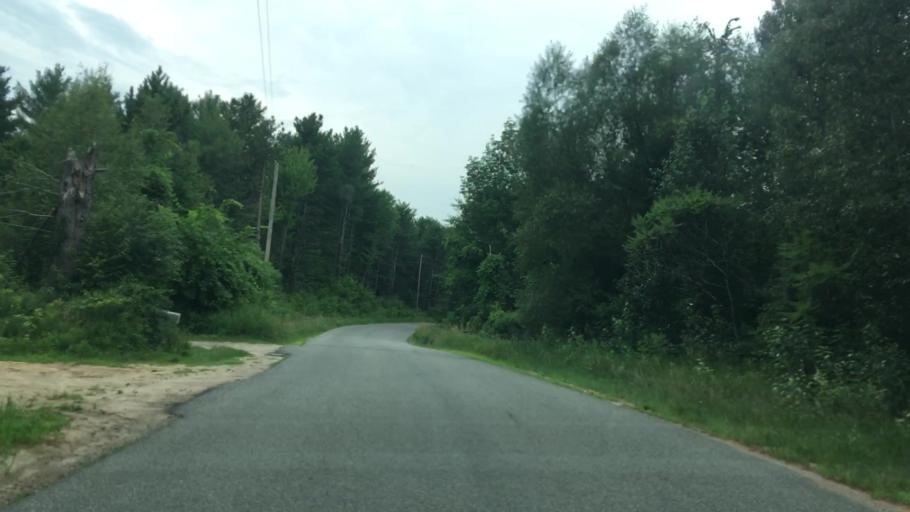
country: US
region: New York
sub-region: Essex County
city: Keeseville
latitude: 44.4461
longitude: -73.6036
